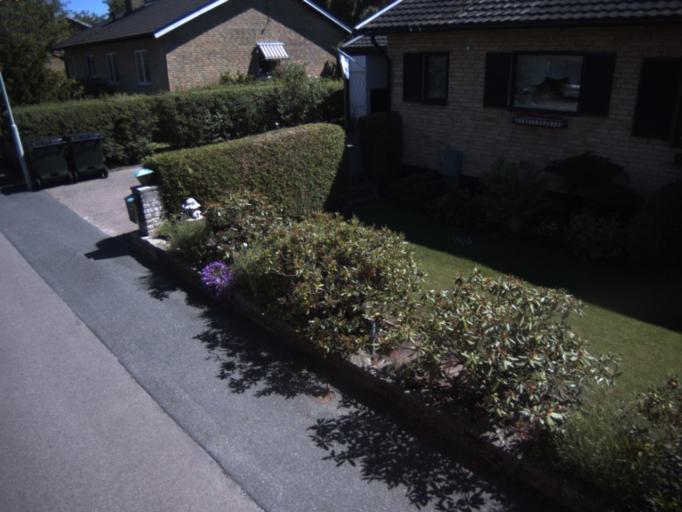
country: SE
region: Skane
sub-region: Helsingborg
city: Morarp
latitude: 56.0618
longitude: 12.8764
